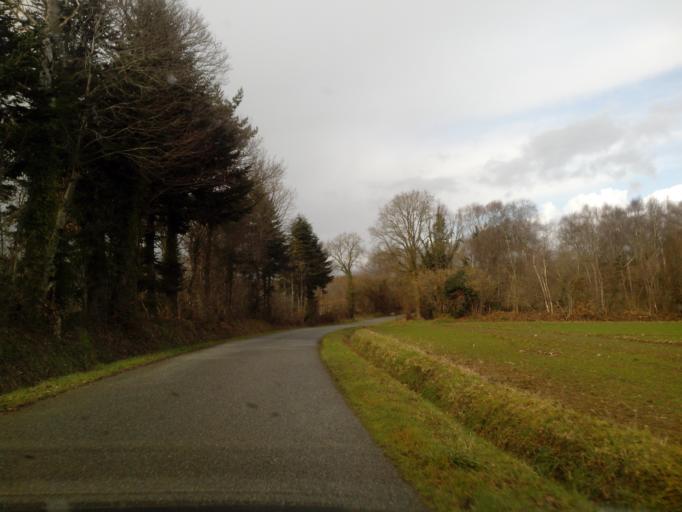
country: FR
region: Brittany
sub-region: Departement des Cotes-d'Armor
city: Merdrignac
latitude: 48.1694
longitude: -2.4196
